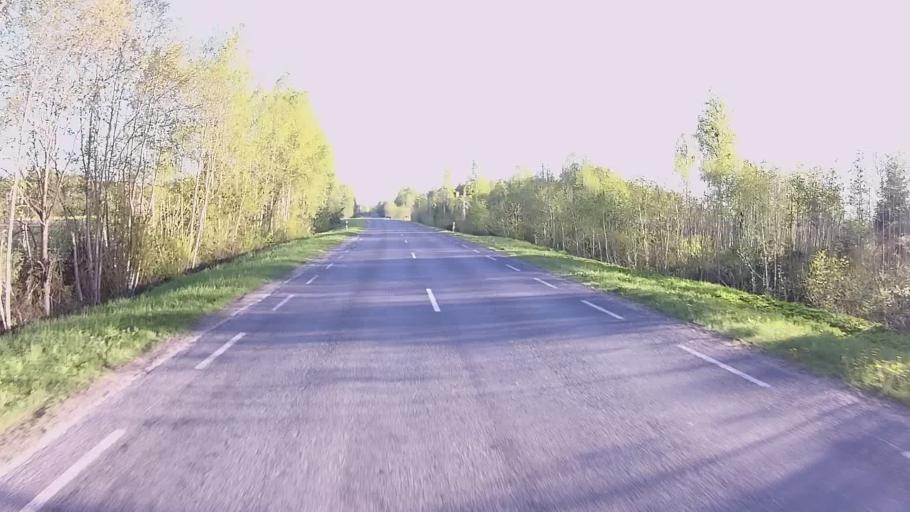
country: EE
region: Viljandimaa
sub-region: Viiratsi vald
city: Viiratsi
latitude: 58.4471
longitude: 25.7377
